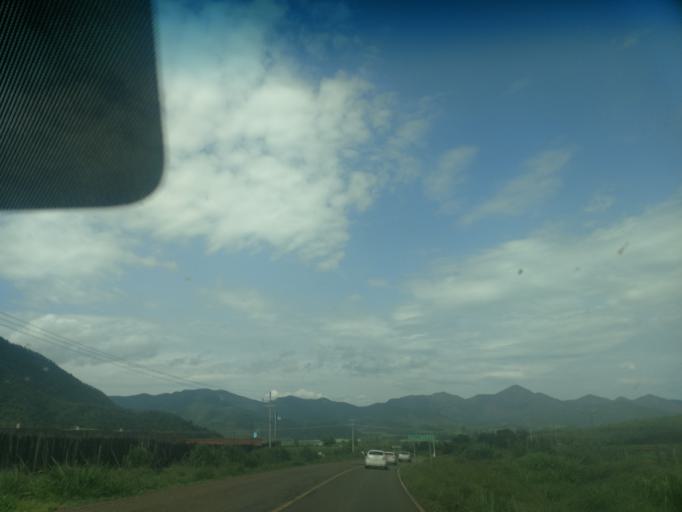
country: MX
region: Jalisco
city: Talpa de Allende
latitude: 20.4215
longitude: -104.7235
